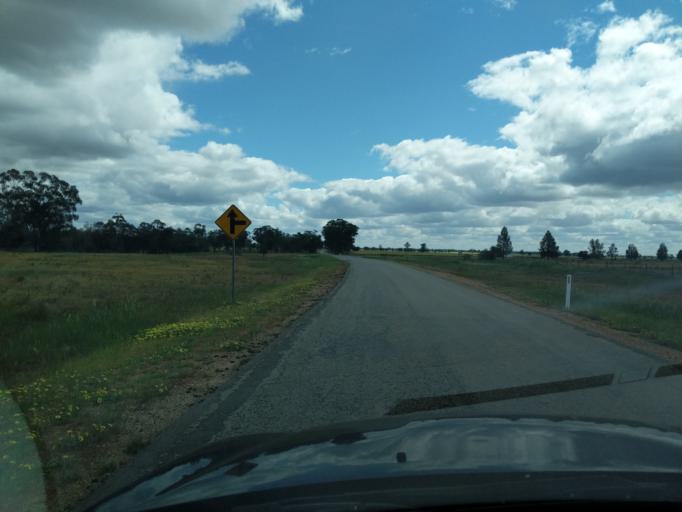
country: AU
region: New South Wales
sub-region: Coolamon
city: Coolamon
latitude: -34.8686
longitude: 146.8981
